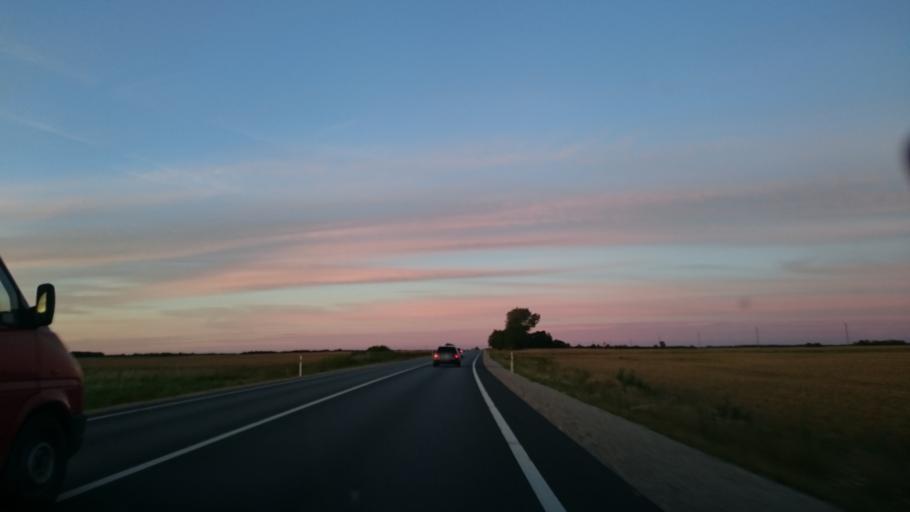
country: LV
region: Dobeles Rajons
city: Dobele
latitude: 56.7344
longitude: 23.2226
